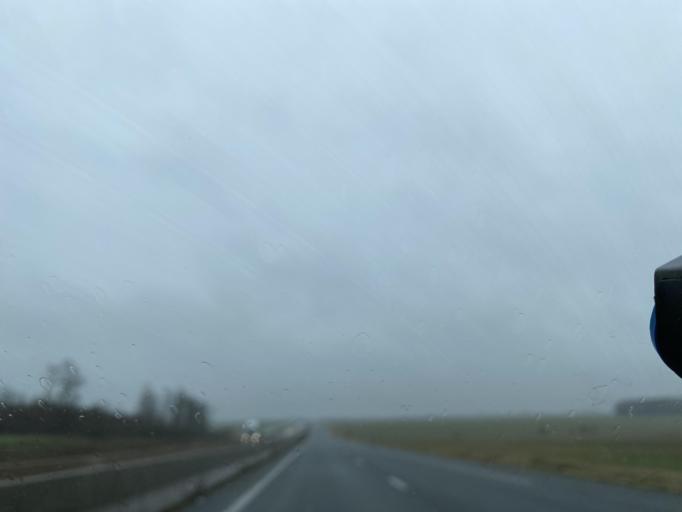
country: FR
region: Centre
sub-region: Departement d'Eure-et-Loir
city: Bailleau-l'Eveque
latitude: 48.5750
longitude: 1.4336
